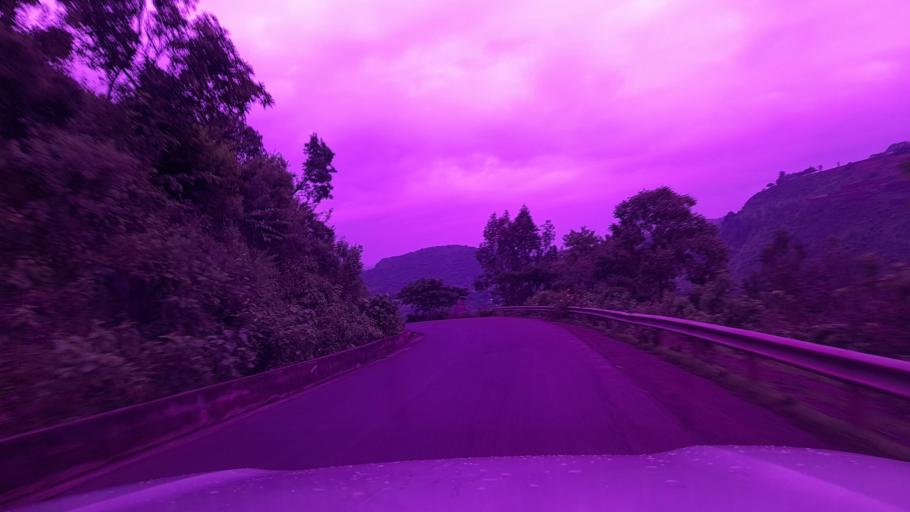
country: ET
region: Oromiya
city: Jima
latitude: 7.9302
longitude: 37.4323
